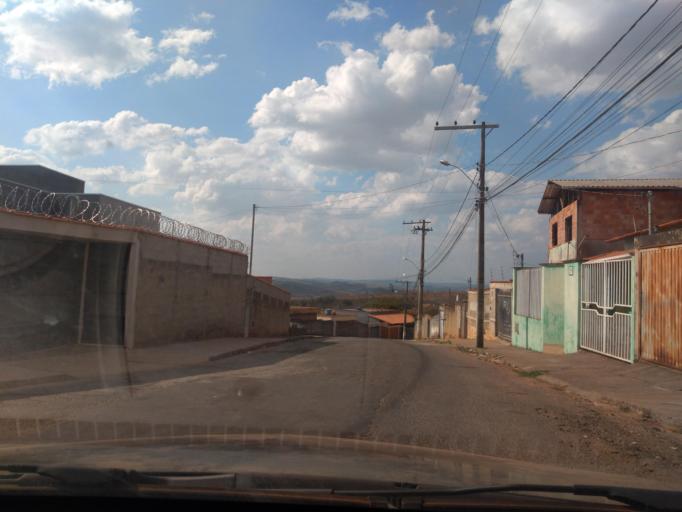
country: BR
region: Minas Gerais
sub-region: Tres Coracoes
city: Tres Coracoes
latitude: -21.6856
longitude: -45.2348
